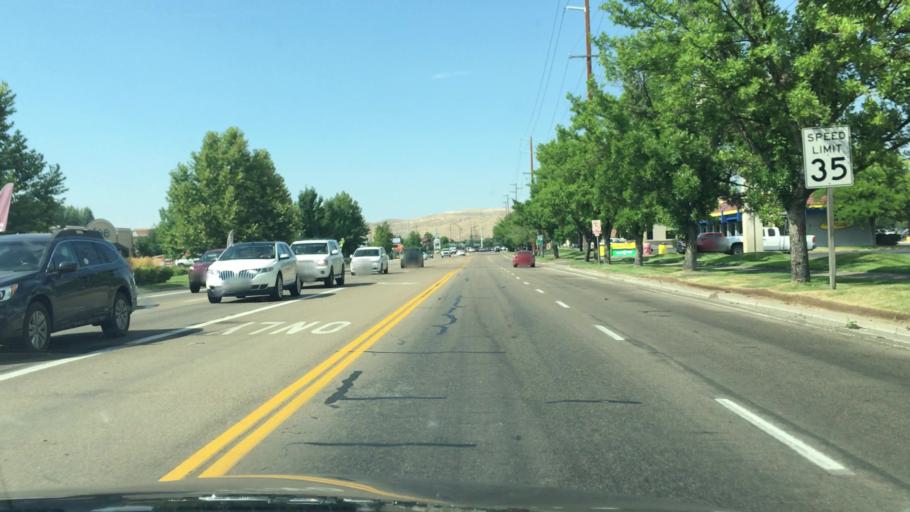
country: US
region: Idaho
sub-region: Ada County
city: Garden City
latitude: 43.6640
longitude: -116.2793
